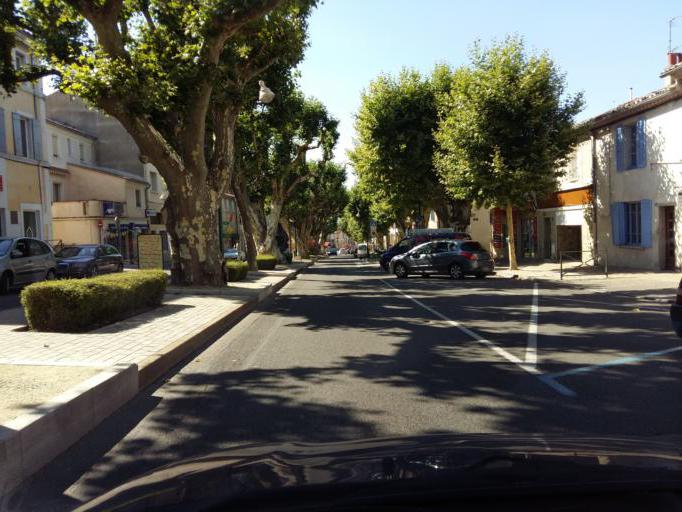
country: FR
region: Provence-Alpes-Cote d'Azur
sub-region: Departement du Vaucluse
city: Valreas
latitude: 44.3850
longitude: 4.9926
